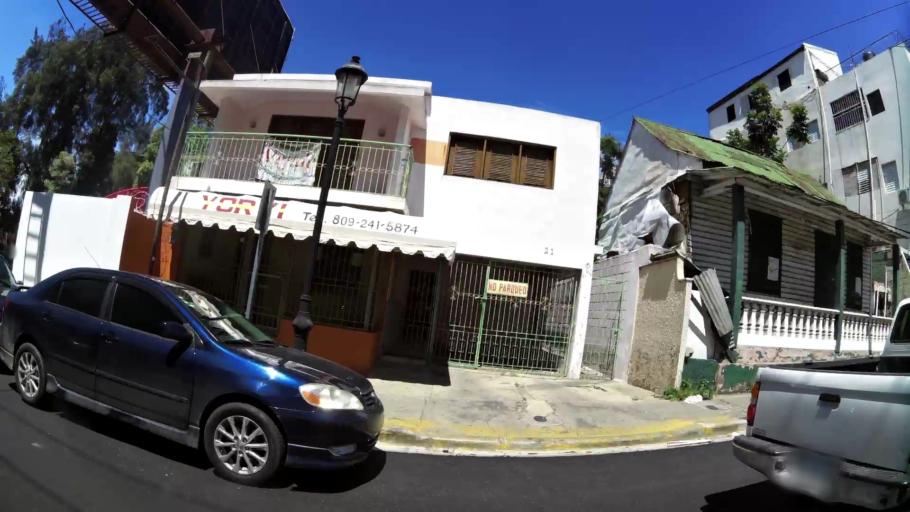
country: DO
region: Santiago
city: Santiago de los Caballeros
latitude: 19.4502
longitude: -70.6981
